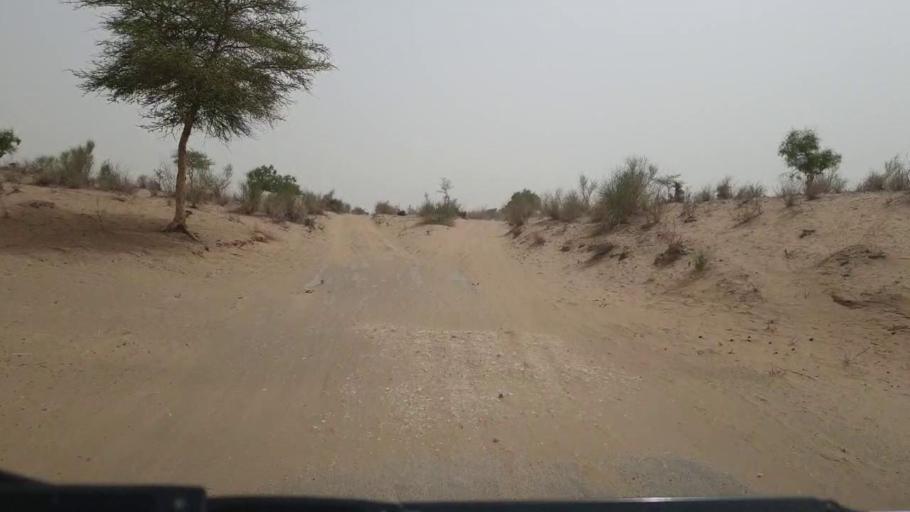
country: PK
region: Sindh
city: Islamkot
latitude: 25.2585
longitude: 70.6421
